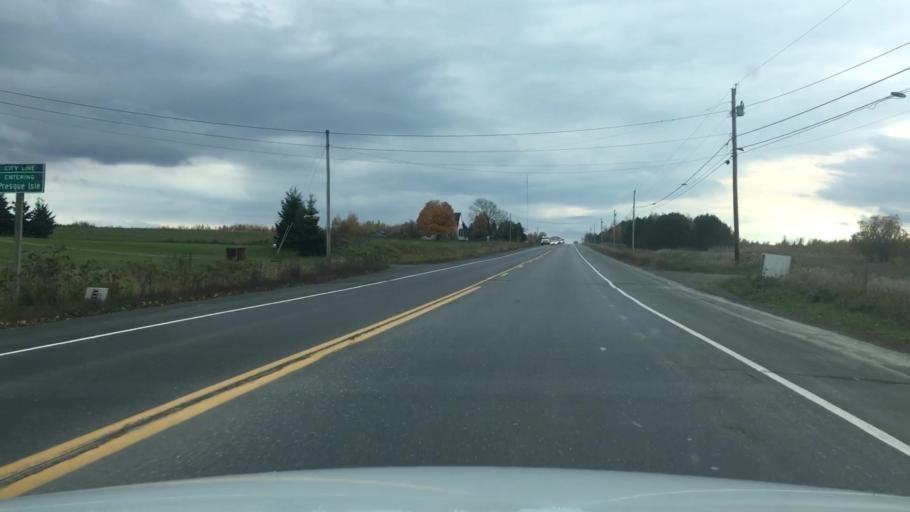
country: US
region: Maine
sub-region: Aroostook County
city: Caribou
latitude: 46.7775
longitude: -67.9893
